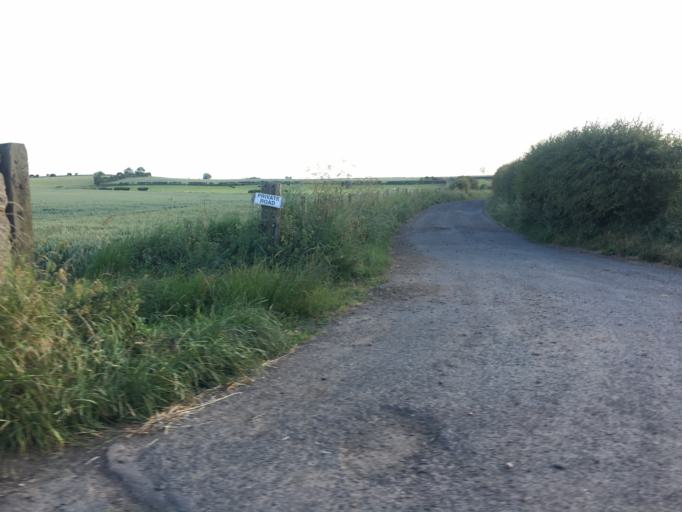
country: GB
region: England
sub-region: Northumberland
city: North Sunderland
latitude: 55.5899
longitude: -1.6838
